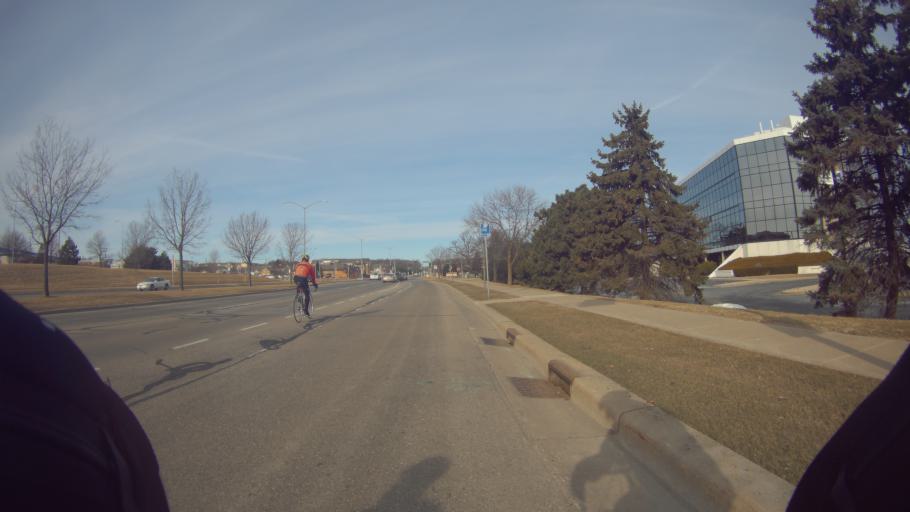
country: US
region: Wisconsin
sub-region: Dane County
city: Middleton
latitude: 43.0751
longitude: -89.5237
